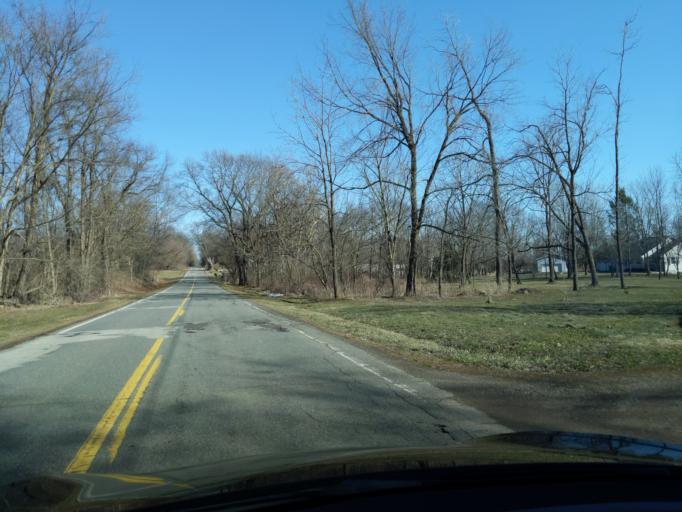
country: US
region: Michigan
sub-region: Ingham County
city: Leslie
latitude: 42.4115
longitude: -84.4230
